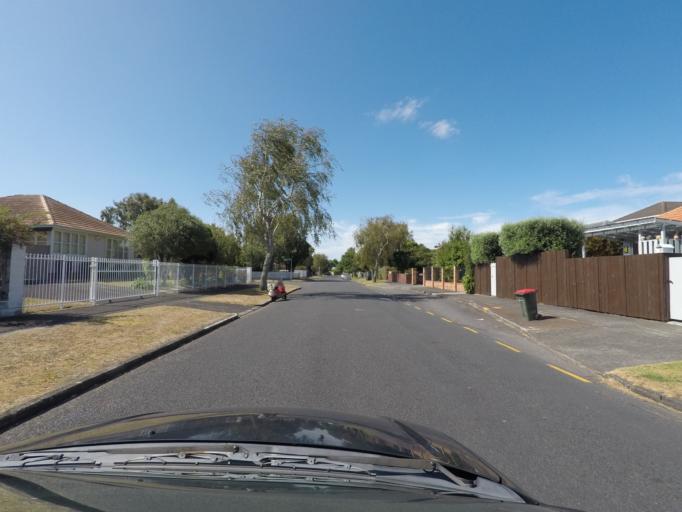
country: NZ
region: Auckland
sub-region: Auckland
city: Rosebank
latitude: -36.8873
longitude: 174.6778
